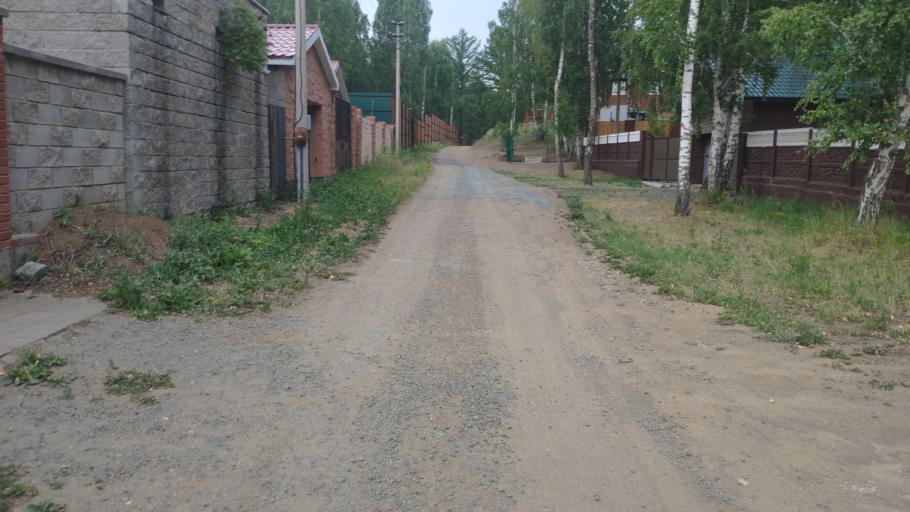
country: RU
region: Bashkortostan
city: Abzakovo
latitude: 53.8029
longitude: 58.6457
